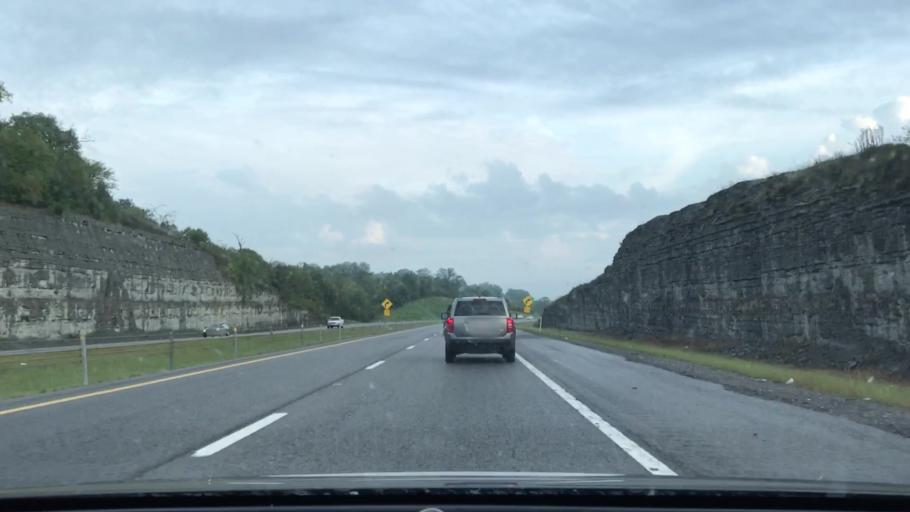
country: US
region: Tennessee
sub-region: Sumner County
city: Shackle Island
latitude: 36.3395
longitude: -86.5497
